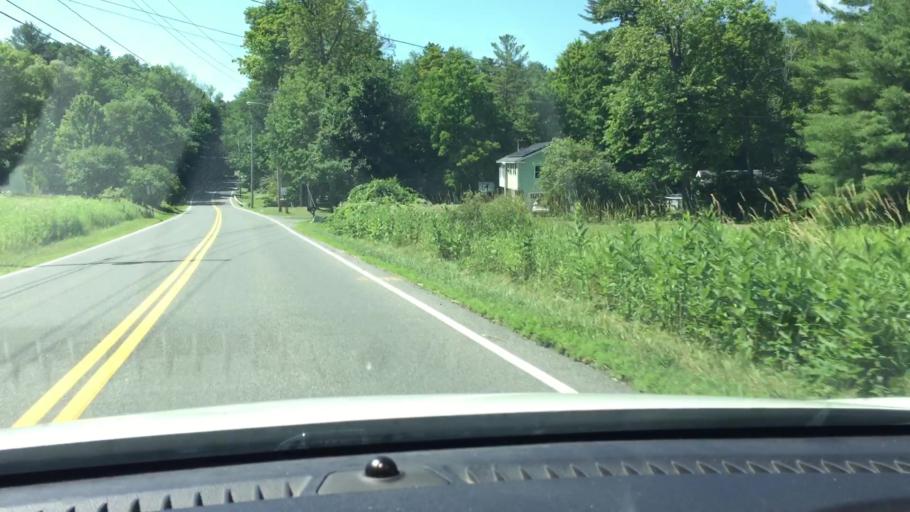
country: US
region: Massachusetts
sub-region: Berkshire County
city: Lenox
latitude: 42.3823
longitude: -73.2566
